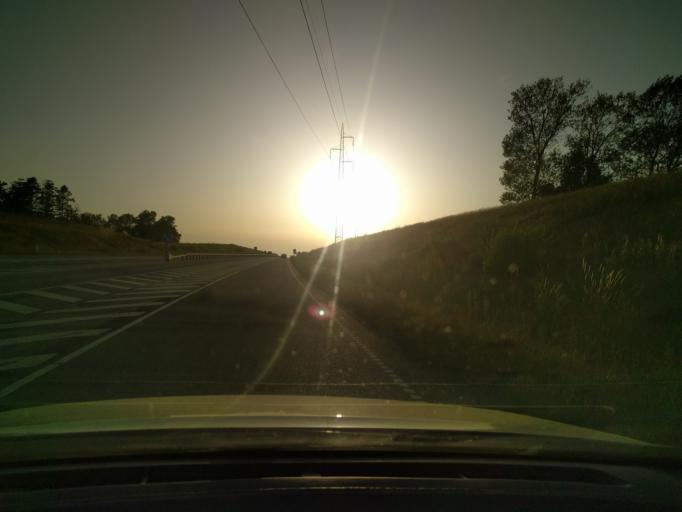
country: DK
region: Zealand
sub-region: Naestved Kommune
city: Fensmark
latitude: 55.2576
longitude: 11.8056
